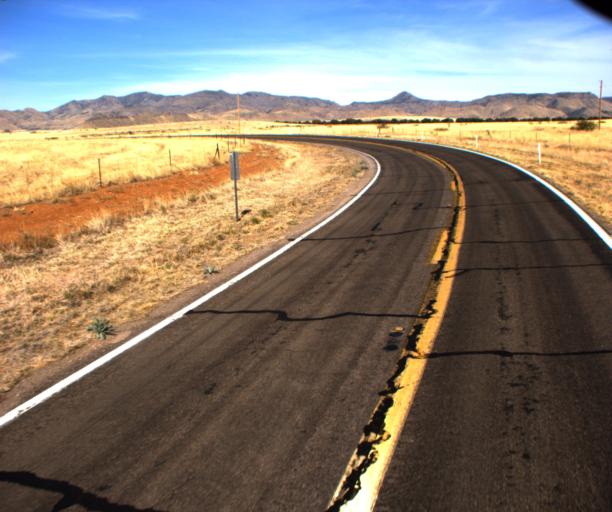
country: US
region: Arizona
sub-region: Cochise County
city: Willcox
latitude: 31.9923
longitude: -109.4416
